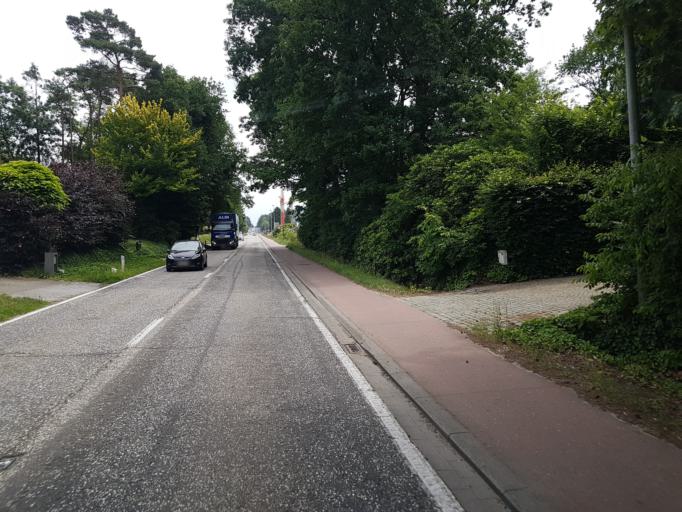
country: BE
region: Flanders
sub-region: Provincie Antwerpen
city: Lille
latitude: 51.2604
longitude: 4.7941
